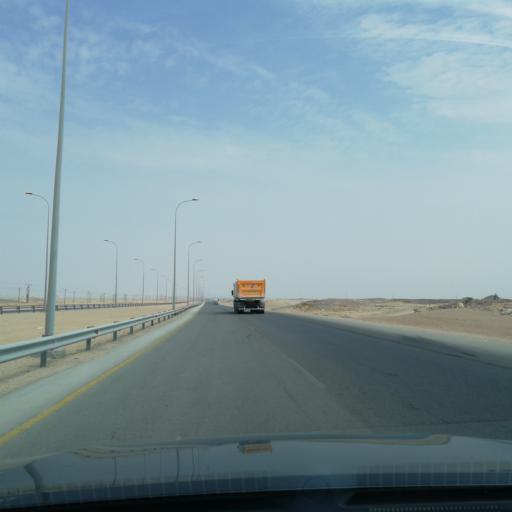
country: OM
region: Zufar
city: Salalah
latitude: 17.5654
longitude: 54.0485
